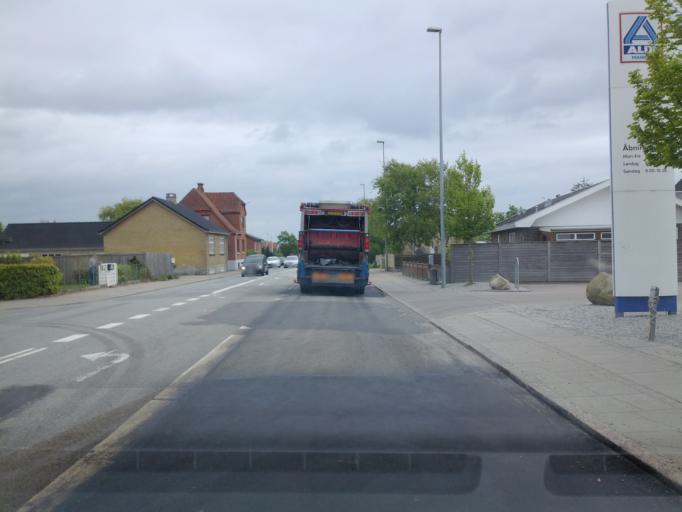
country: DK
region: North Denmark
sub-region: Frederikshavn Kommune
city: Frederikshavn
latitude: 57.4273
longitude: 10.5141
